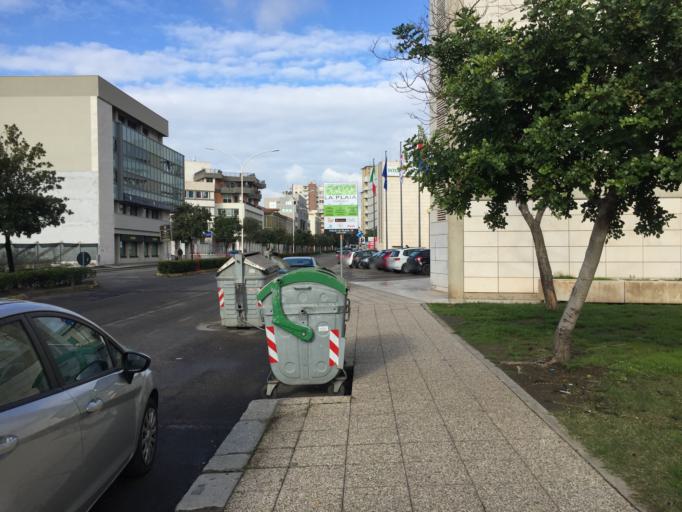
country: IT
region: Sardinia
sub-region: Provincia di Cagliari
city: Cagliari
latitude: 39.2091
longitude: 9.1218
